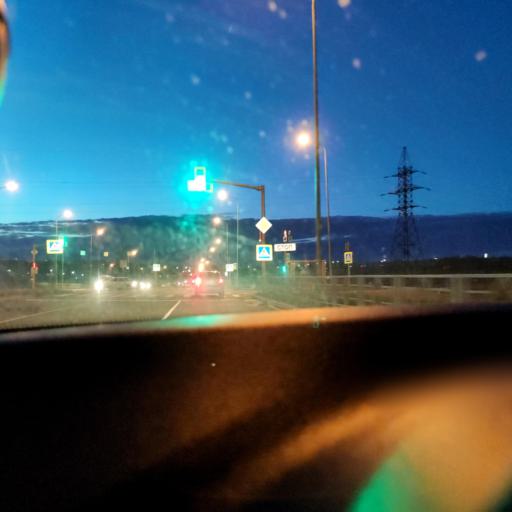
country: RU
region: Samara
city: Petra-Dubrava
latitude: 53.2984
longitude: 50.3206
